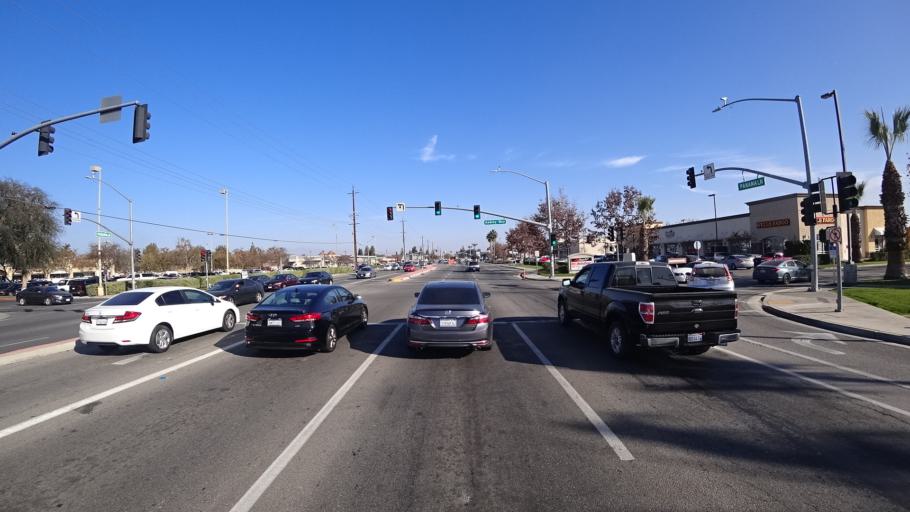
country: US
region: California
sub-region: Kern County
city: Greenfield
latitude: 35.2958
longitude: -119.0411
